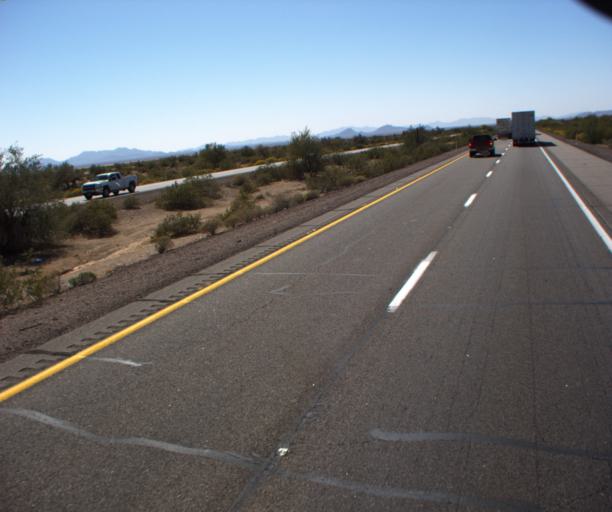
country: US
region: Arizona
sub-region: Yuma County
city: Wellton
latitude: 32.7208
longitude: -113.7749
